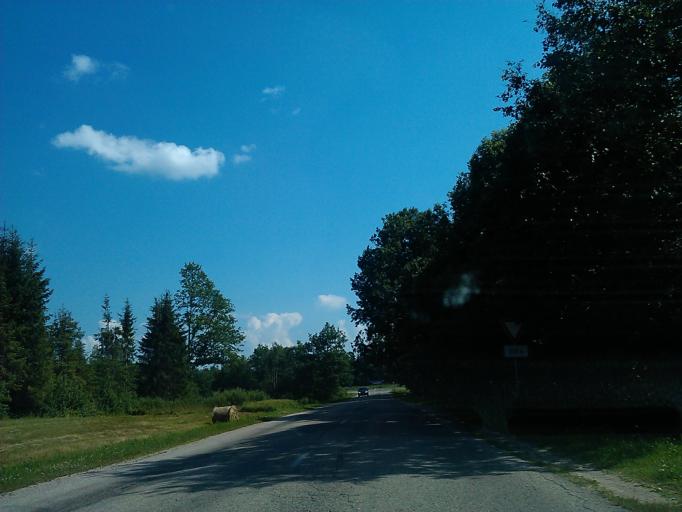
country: LV
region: Aizpute
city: Aizpute
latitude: 56.6025
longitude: 21.7413
